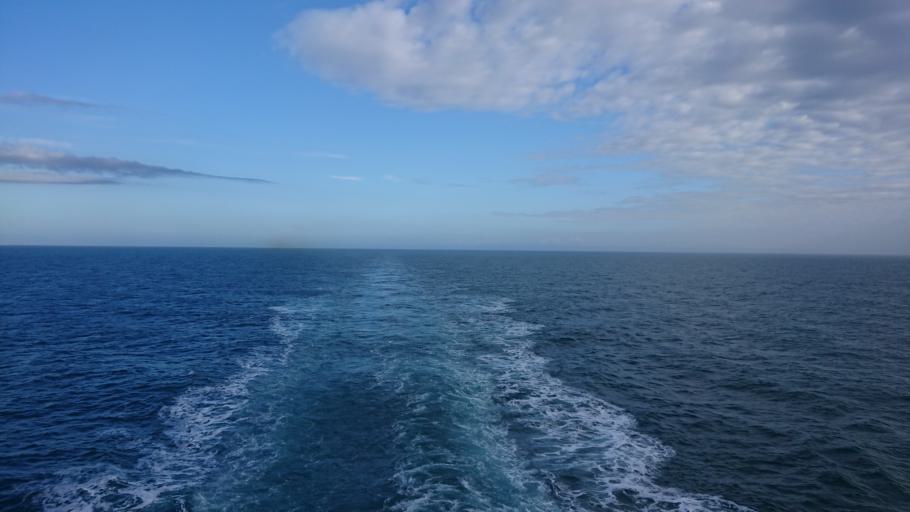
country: GB
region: Wales
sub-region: Pembrokeshire
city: Saint David's
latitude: 52.1345
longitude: -5.6157
